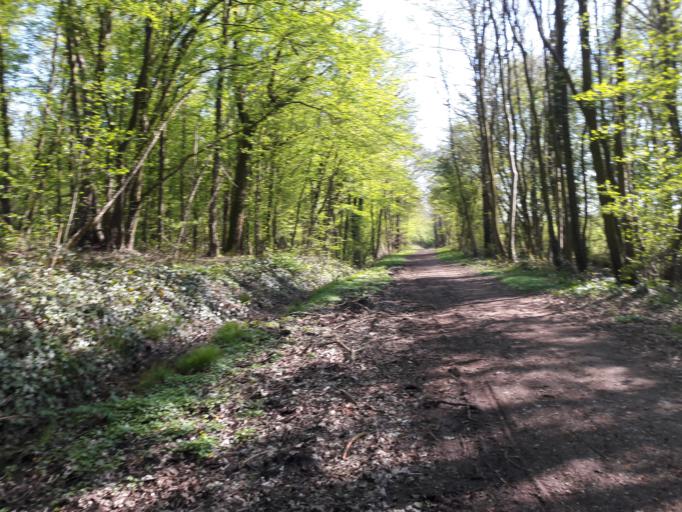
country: FR
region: Nord-Pas-de-Calais
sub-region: Departement du Nord
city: Sains-du-Nord
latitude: 50.1460
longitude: 4.0683
